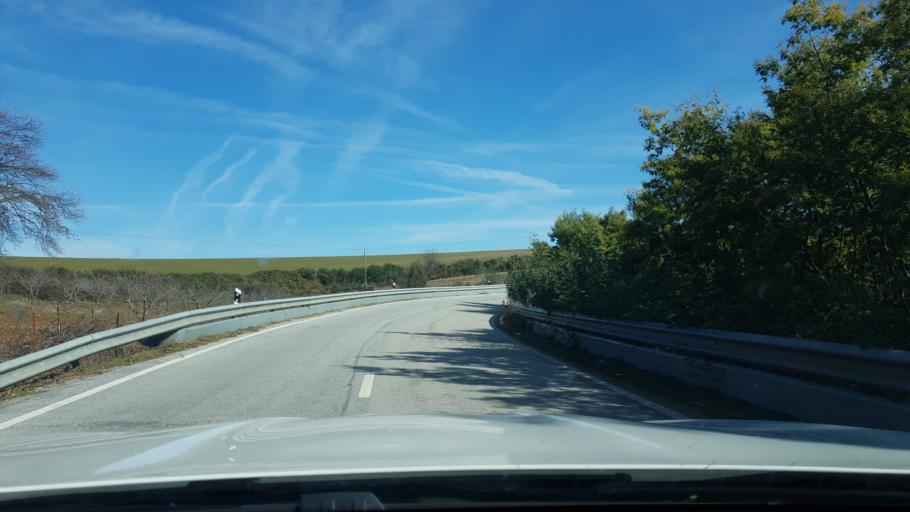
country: PT
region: Braganca
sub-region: Torre de Moncorvo
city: Torre de Moncorvo
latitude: 41.1801
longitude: -6.9321
